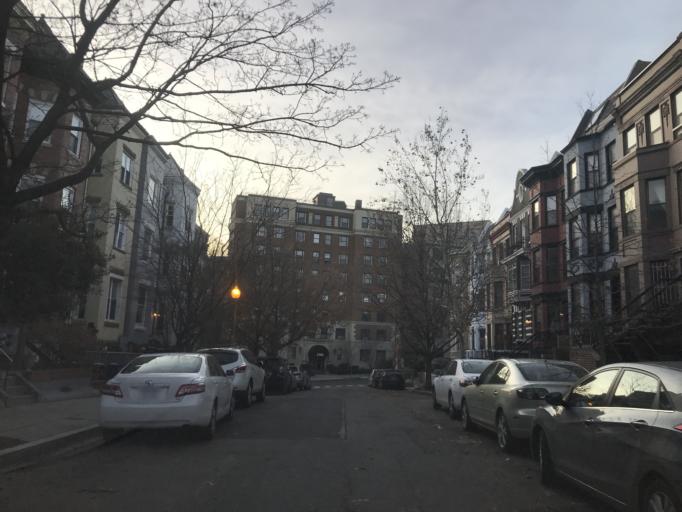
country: US
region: Washington, D.C.
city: Washington, D.C.
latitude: 38.9178
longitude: -77.0435
